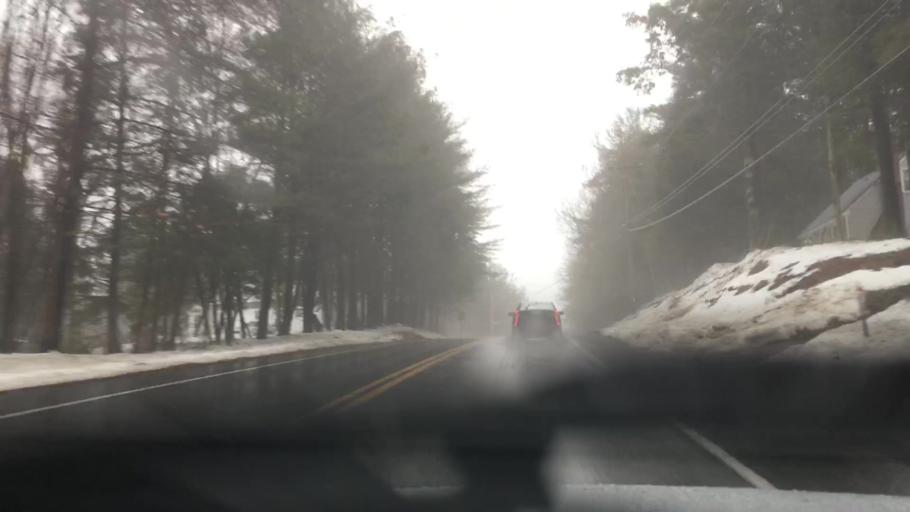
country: US
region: Massachusetts
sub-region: Franklin County
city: Wendell
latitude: 42.5025
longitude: -72.3367
